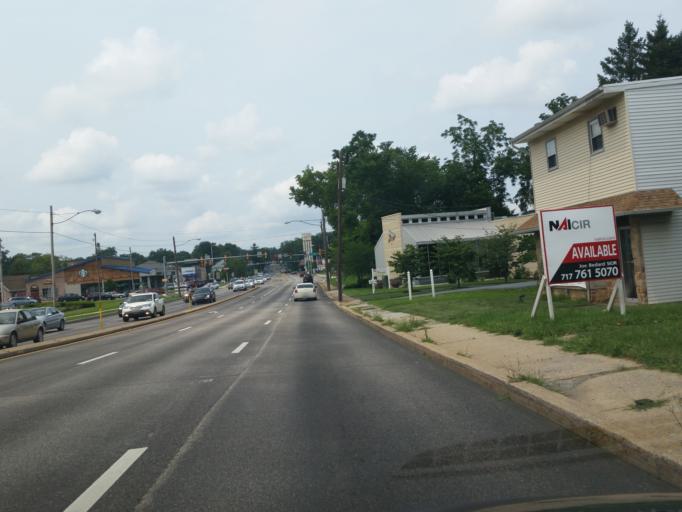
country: US
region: Pennsylvania
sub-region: Cumberland County
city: Camp Hill
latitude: 40.2373
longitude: -76.9339
